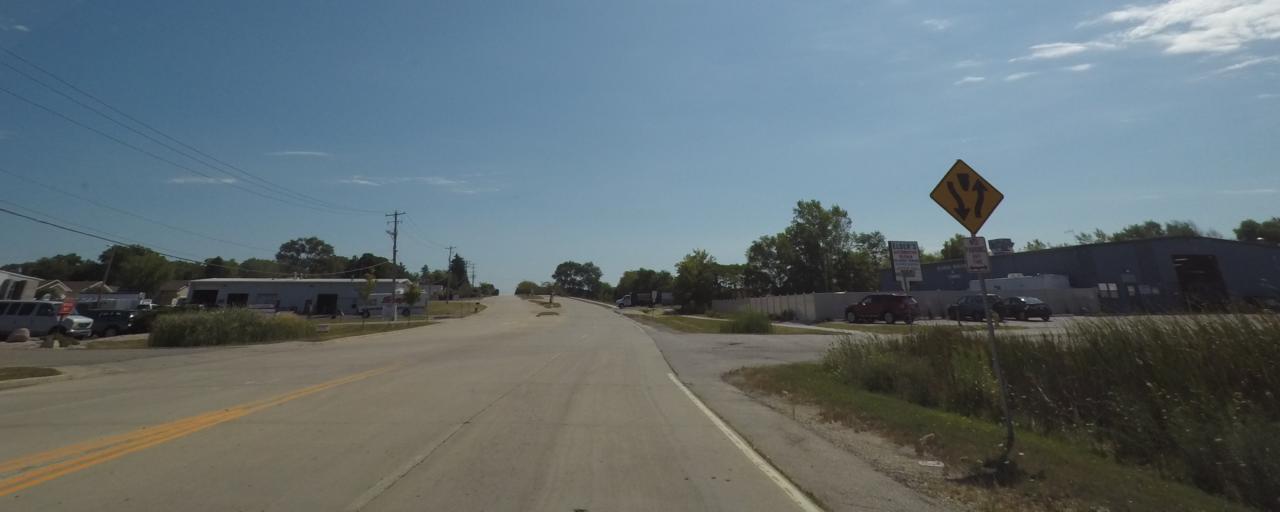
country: US
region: Wisconsin
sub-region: Waukesha County
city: Waukesha
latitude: 43.0139
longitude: -88.2075
